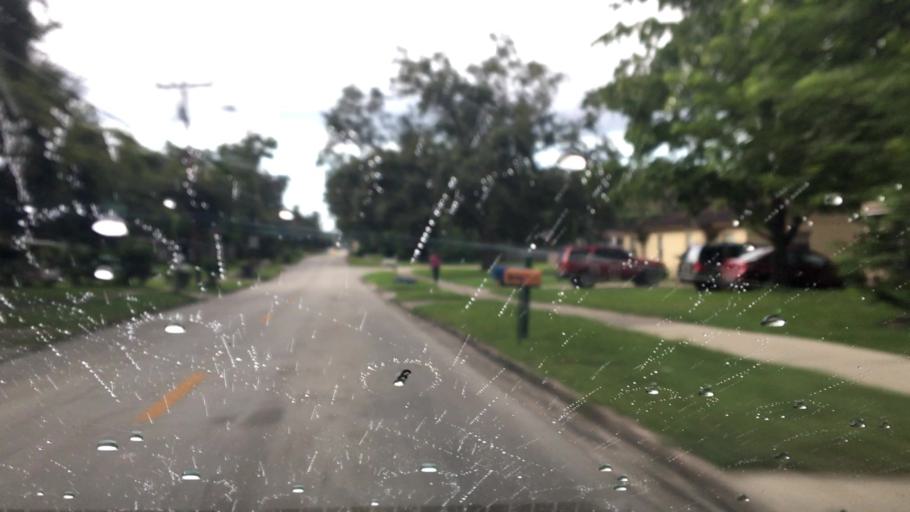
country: US
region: Florida
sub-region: Seminole County
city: Sanford
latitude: 28.7961
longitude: -81.2560
